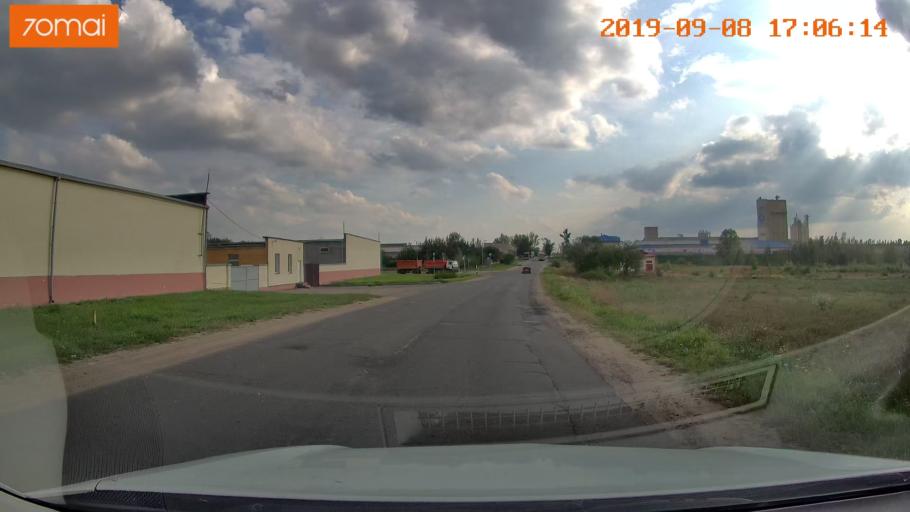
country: BY
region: Grodnenskaya
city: Hrodna
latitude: 53.6722
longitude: 23.9532
